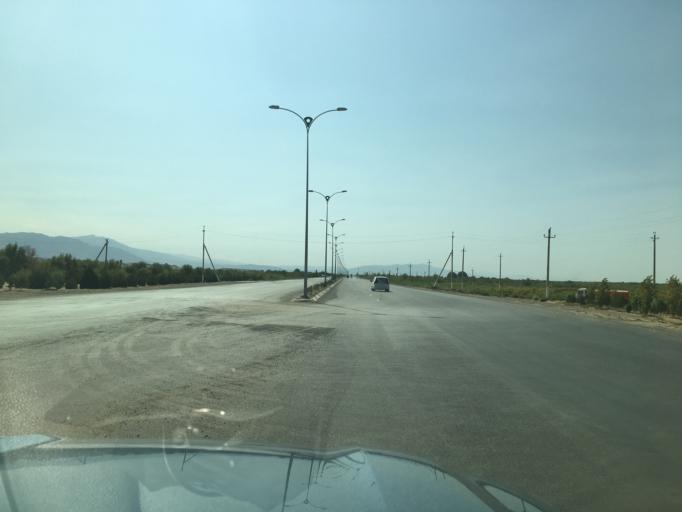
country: TM
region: Ahal
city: Abadan
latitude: 38.1028
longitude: 58.3057
